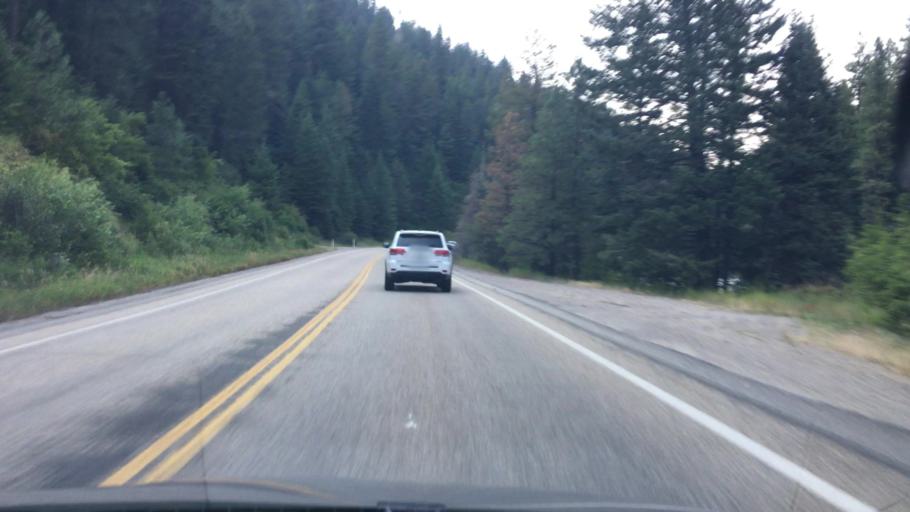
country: US
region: Idaho
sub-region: Valley County
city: Cascade
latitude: 44.1883
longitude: -116.1147
